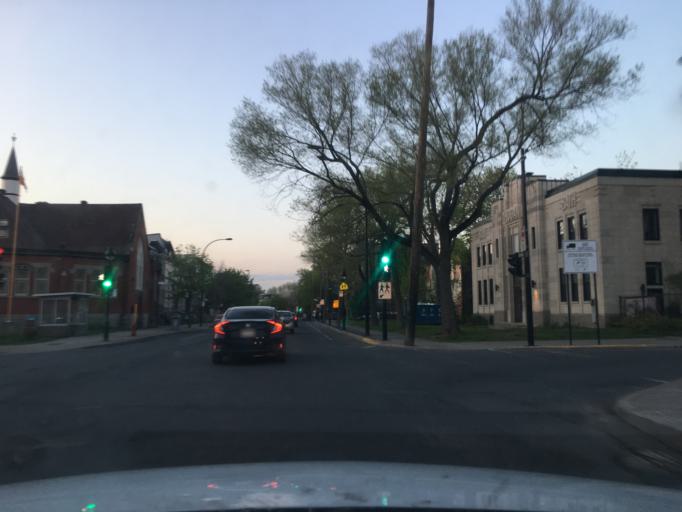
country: CA
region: Quebec
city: Westmount
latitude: 45.4762
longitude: -73.5600
